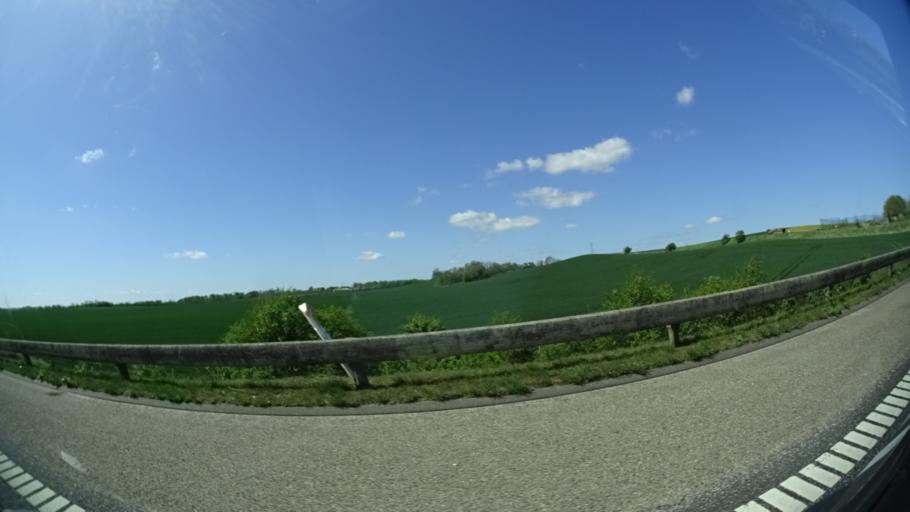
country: DK
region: Central Jutland
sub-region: Arhus Kommune
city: Framlev
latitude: 56.1664
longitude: 10.0502
